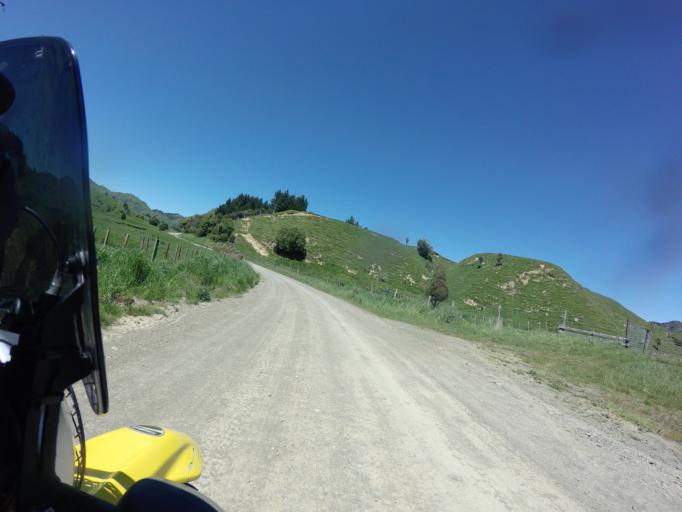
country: NZ
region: Bay of Plenty
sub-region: Opotiki District
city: Opotiki
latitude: -38.3908
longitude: 177.4590
